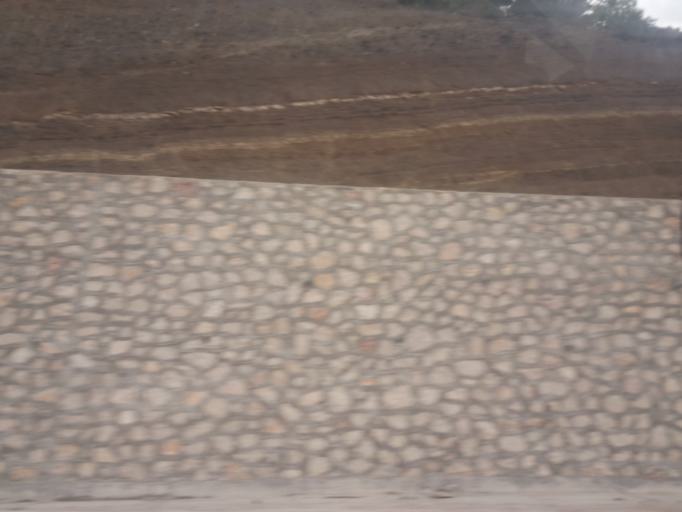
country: TR
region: Tokat
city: Bereketli
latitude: 40.5401
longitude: 37.3085
